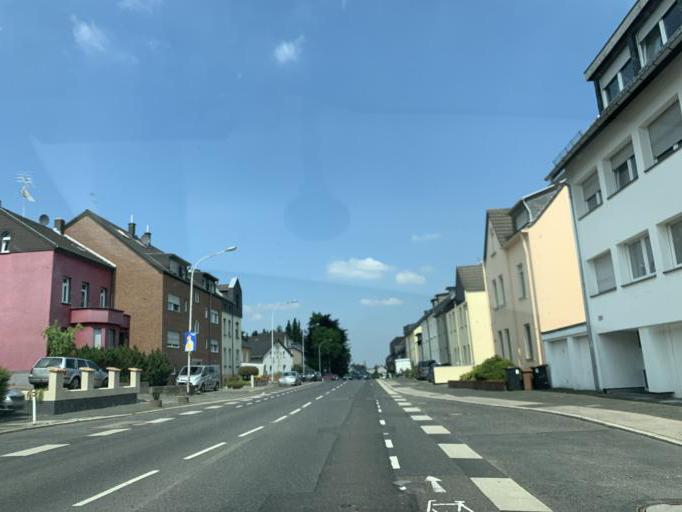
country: DE
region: North Rhine-Westphalia
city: Bruhl
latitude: 50.8105
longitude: 6.8839
